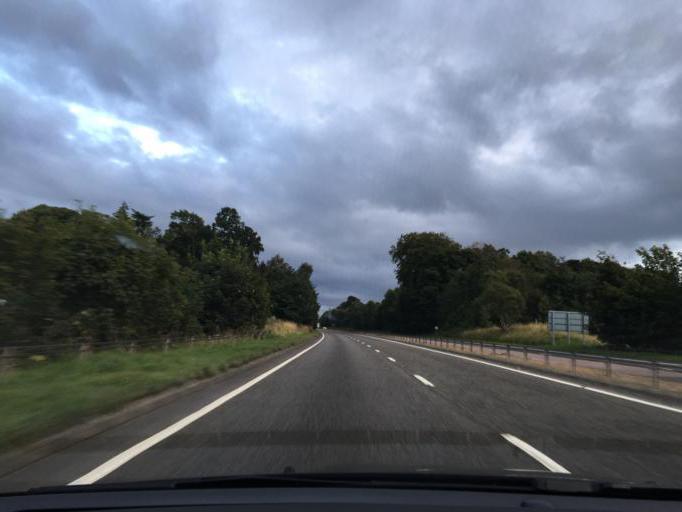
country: GB
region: Scotland
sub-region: Highland
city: Inverness
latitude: 57.4674
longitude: -4.1786
